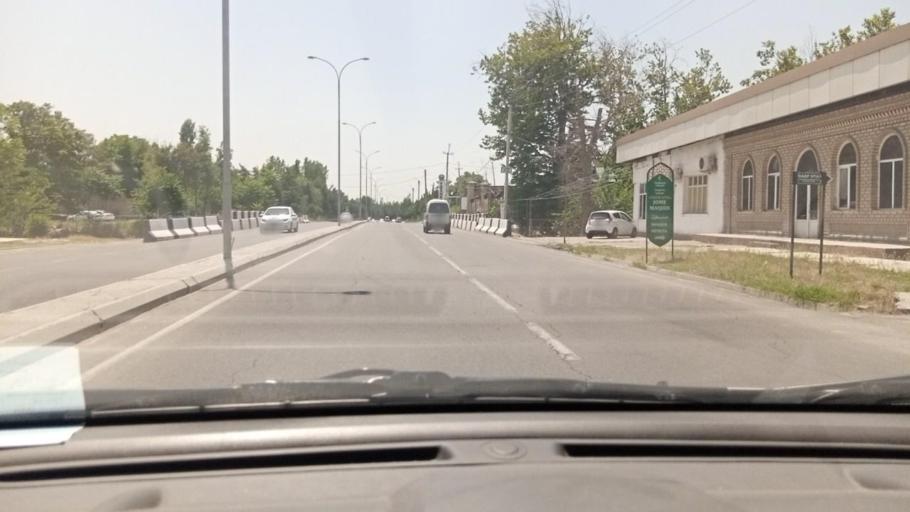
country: UZ
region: Toshkent
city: Urtaowul
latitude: 41.2202
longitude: 69.1752
